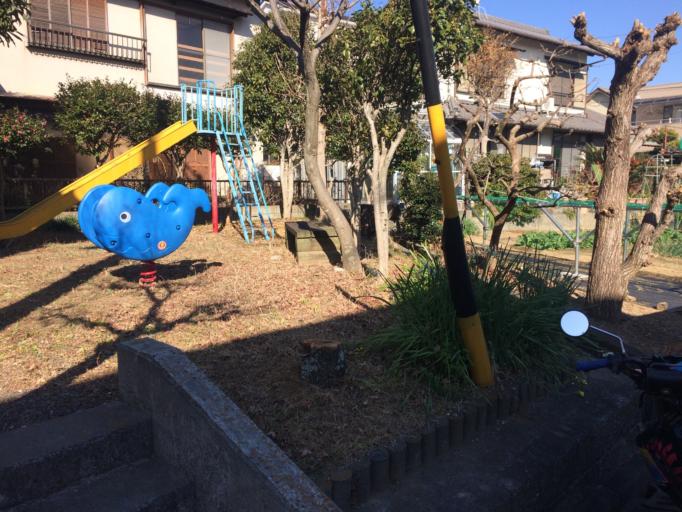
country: JP
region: Shizuoka
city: Shizuoka-shi
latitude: 35.0334
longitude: 138.4876
